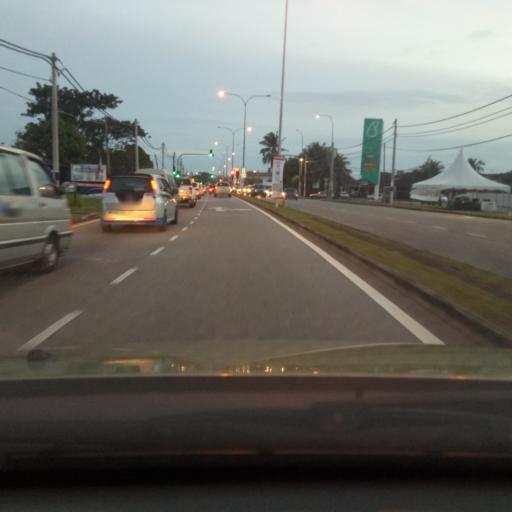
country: MY
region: Kedah
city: Alor Setar
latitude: 6.1079
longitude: 100.3728
